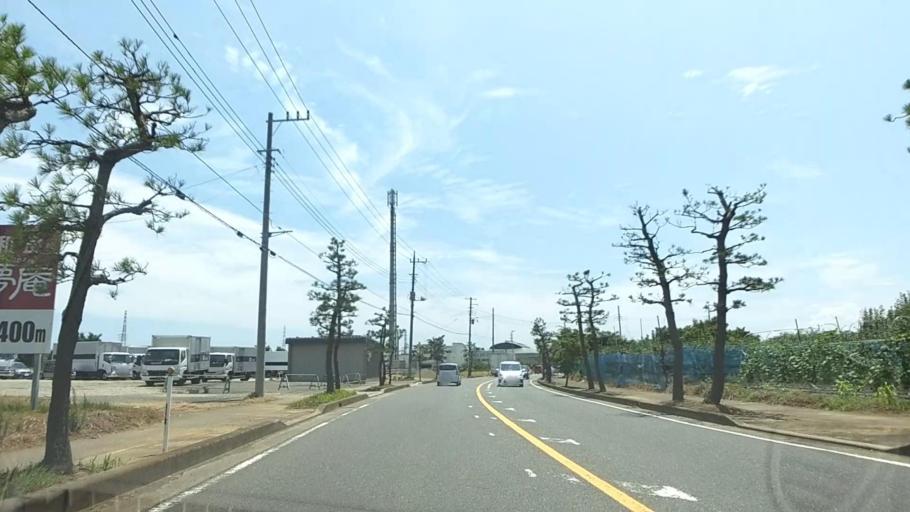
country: JP
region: Kanagawa
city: Chigasaki
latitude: 35.3799
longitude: 139.3856
